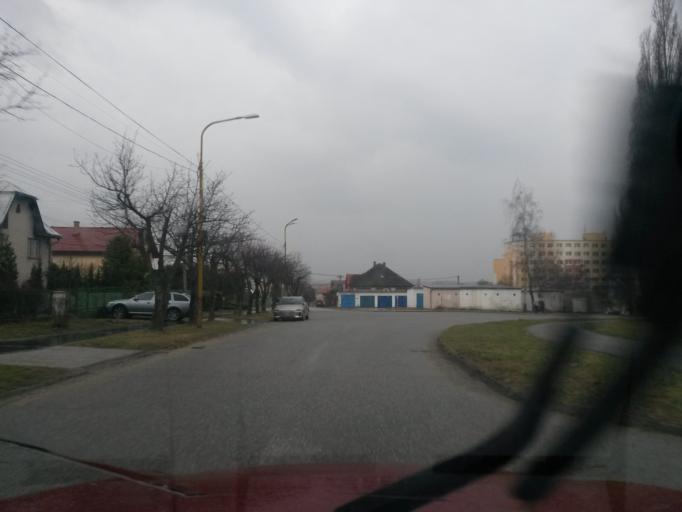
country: SK
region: Kosicky
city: Kosice
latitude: 48.7356
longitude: 21.2918
